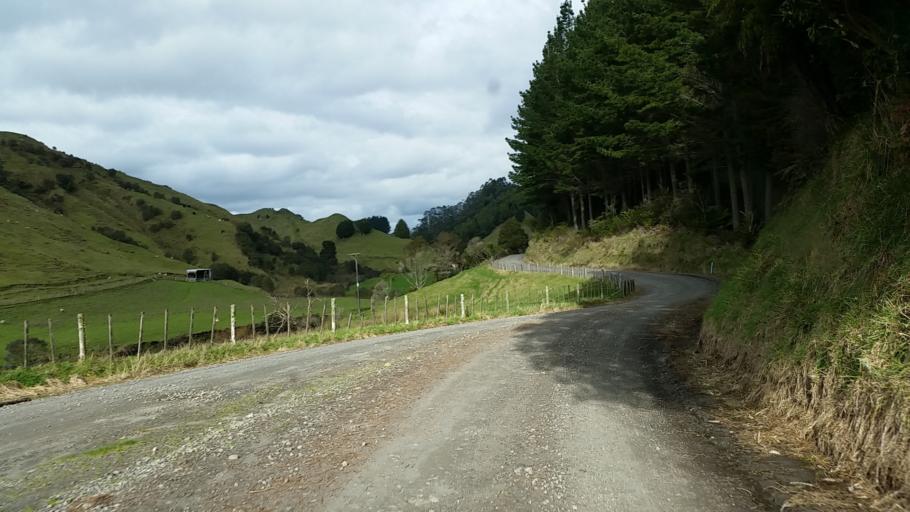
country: NZ
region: Taranaki
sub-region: New Plymouth District
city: Waitara
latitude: -39.1554
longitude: 174.5604
